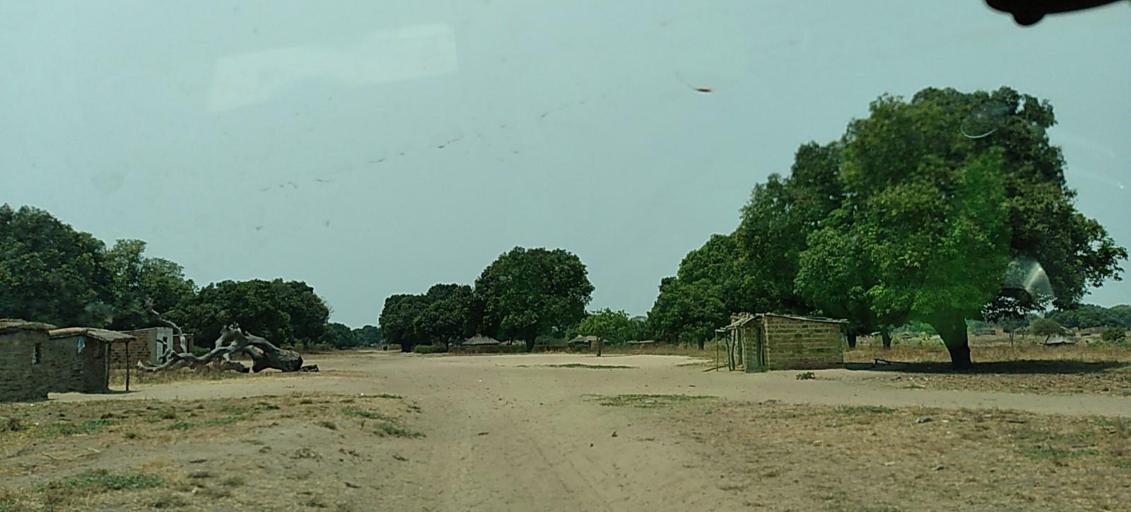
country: ZM
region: Western
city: Lukulu
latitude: -14.1582
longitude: 23.3100
